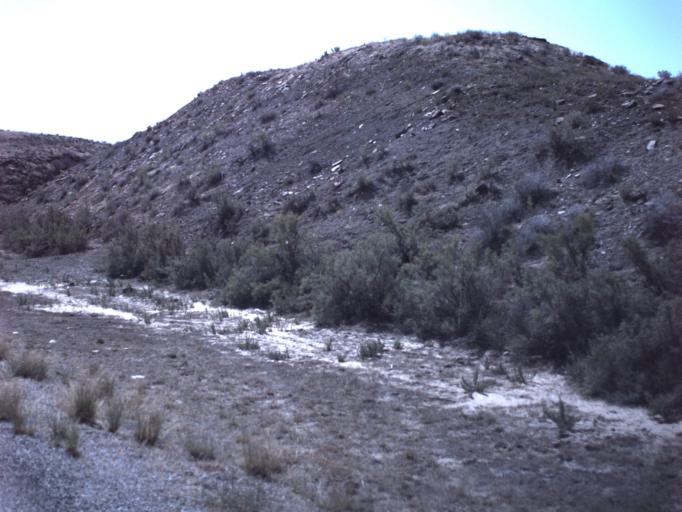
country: US
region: Utah
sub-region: Grand County
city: Moab
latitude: 38.8558
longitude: -109.2888
